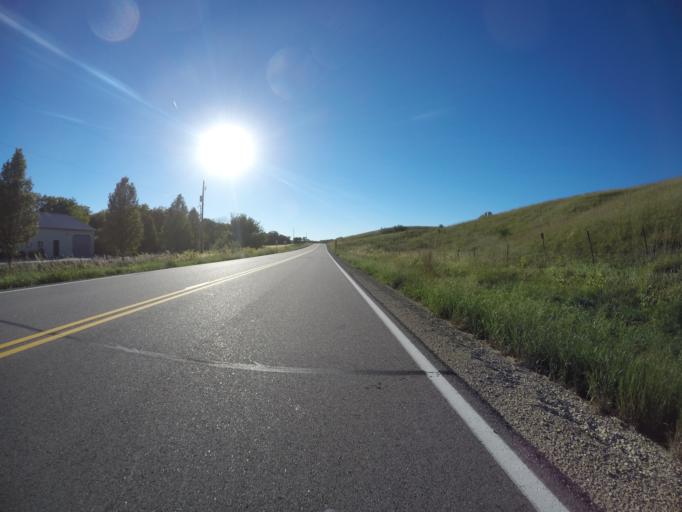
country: US
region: Kansas
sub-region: Riley County
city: Ogden
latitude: 39.2319
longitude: -96.7476
